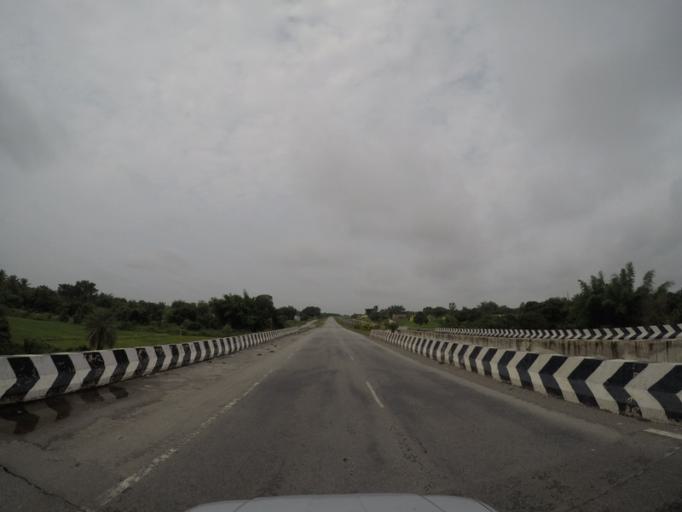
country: IN
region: Karnataka
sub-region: Tumkur
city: Kunigal
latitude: 13.0022
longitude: 76.9683
